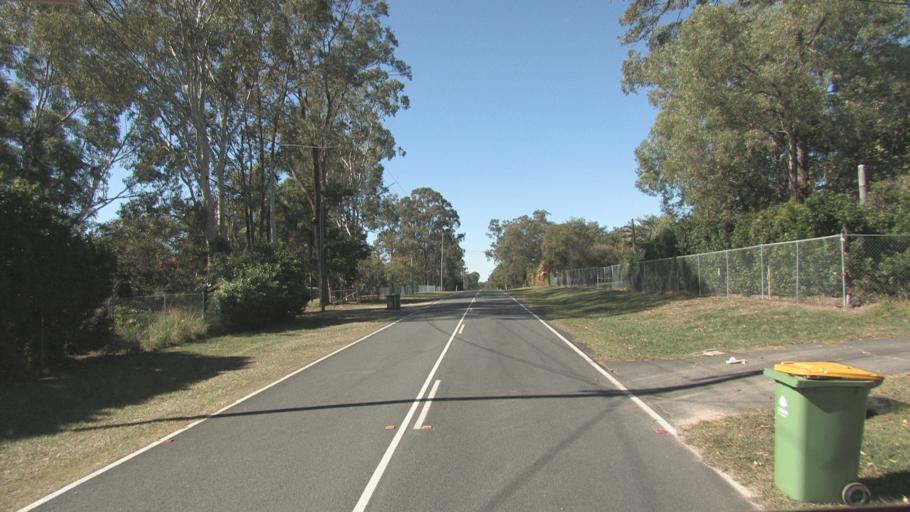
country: AU
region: Queensland
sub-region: Logan
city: Park Ridge South
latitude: -27.7067
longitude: 153.0429
